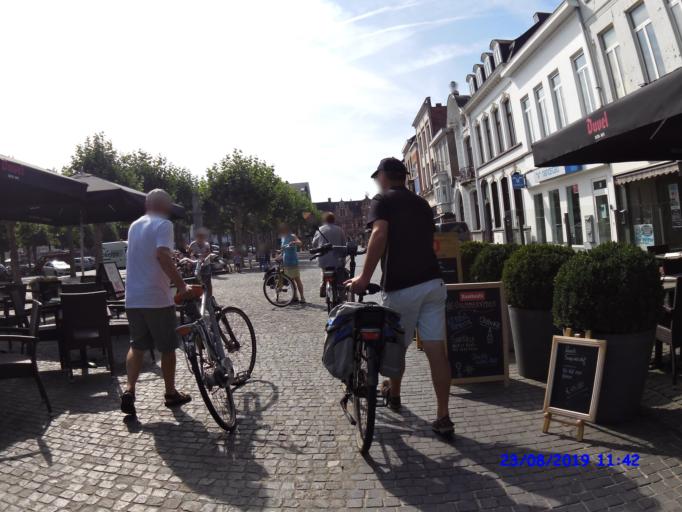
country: BE
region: Flanders
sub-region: Provincie Oost-Vlaanderen
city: Lokeren
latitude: 51.1048
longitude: 3.9891
